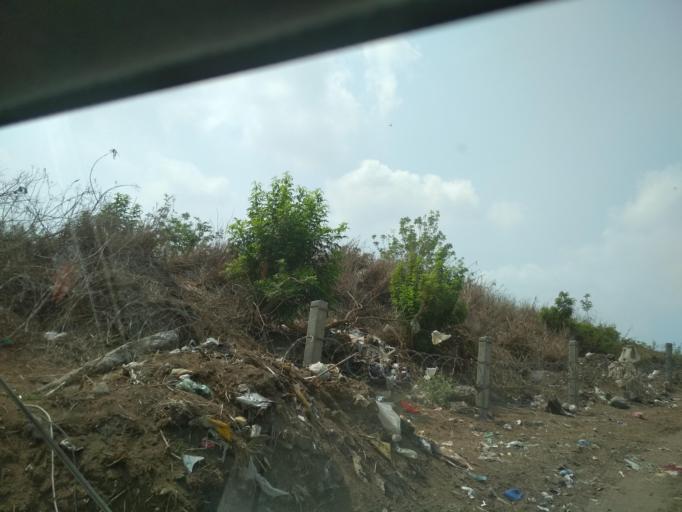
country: MX
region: Veracruz
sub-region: Veracruz
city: Arboledas
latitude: 19.2088
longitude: -96.2134
